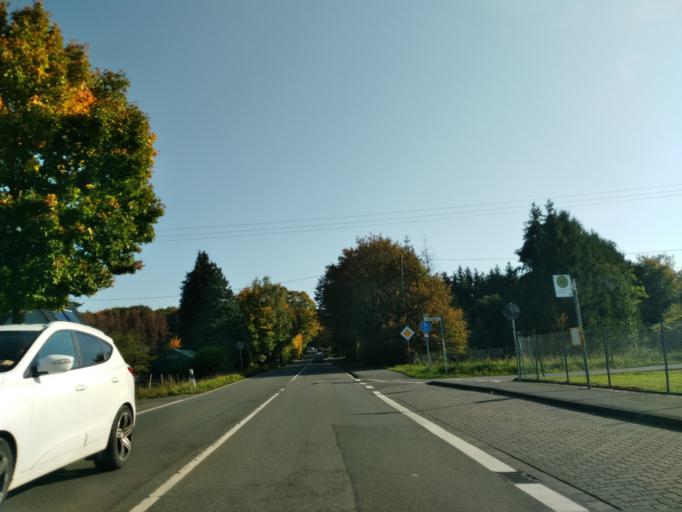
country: DE
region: North Rhine-Westphalia
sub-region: Regierungsbezirk Koln
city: Hennef
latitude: 50.7459
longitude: 7.3453
